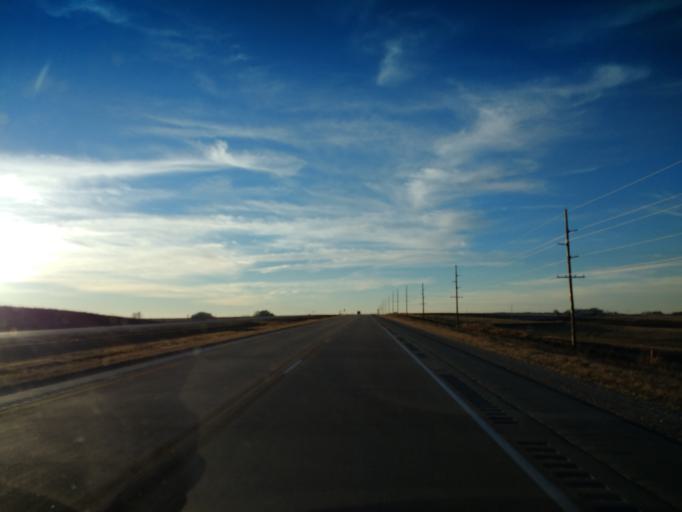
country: US
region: Iowa
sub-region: Ida County
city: Holstein
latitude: 42.4751
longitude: -95.4811
